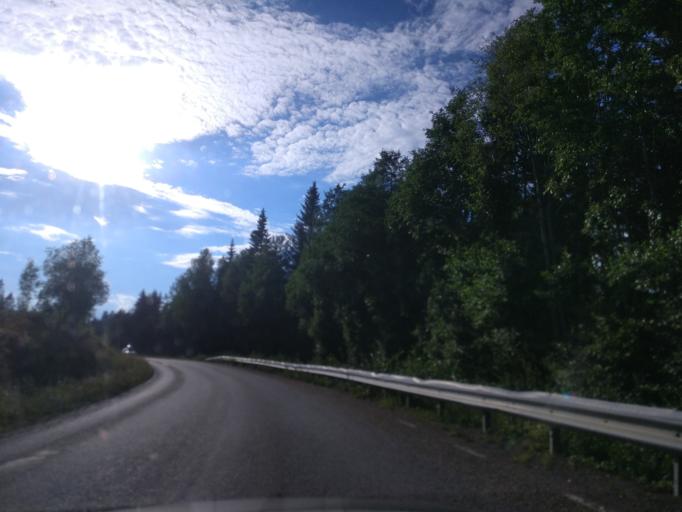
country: SE
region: Dalarna
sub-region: Ludvika Kommun
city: Ludvika
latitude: 60.2923
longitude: 15.1257
